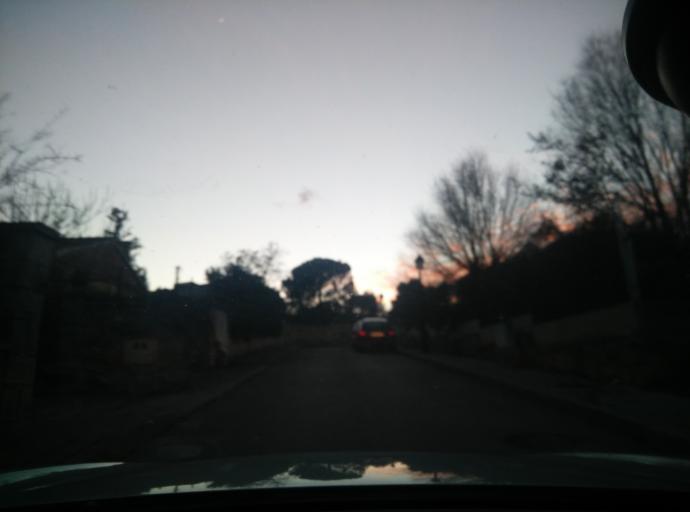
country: ES
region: Madrid
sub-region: Provincia de Madrid
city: Manzanares el Real
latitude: 40.7355
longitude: -3.8544
